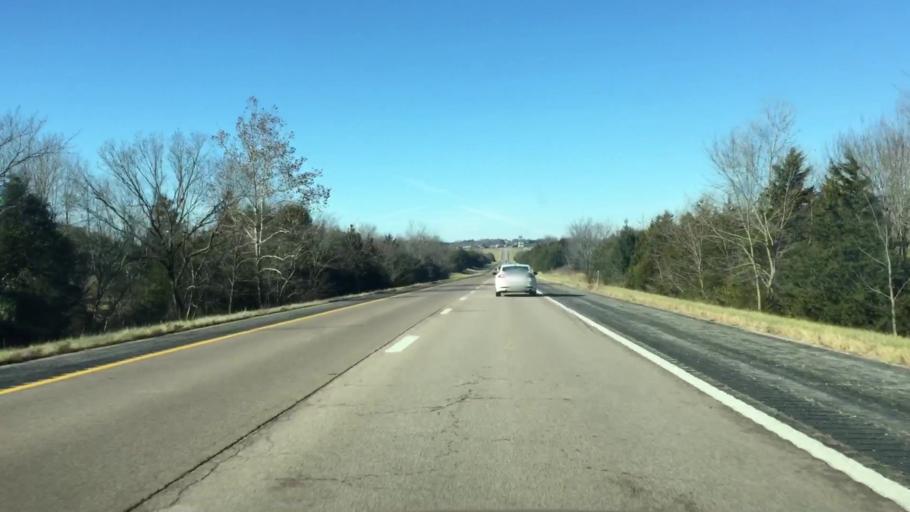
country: US
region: Missouri
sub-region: Miller County
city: Eldon
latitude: 38.3677
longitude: -92.4832
